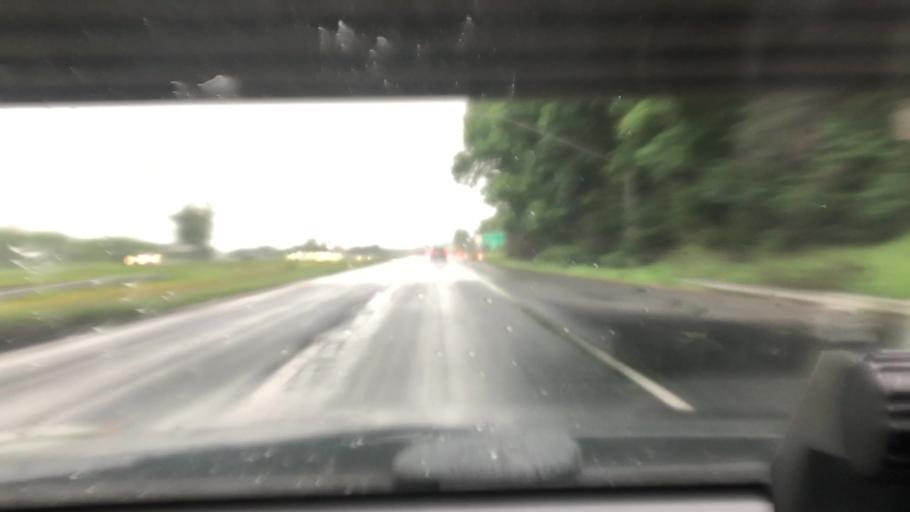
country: US
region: Pennsylvania
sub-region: Northampton County
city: Palmer Heights
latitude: 40.6973
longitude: -75.2897
